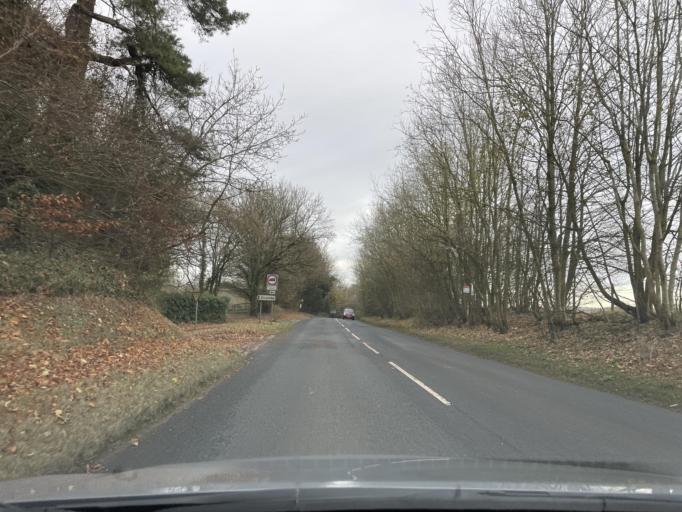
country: GB
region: England
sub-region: Borough of Swindon
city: Wroughton
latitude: 51.5177
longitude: -1.8078
